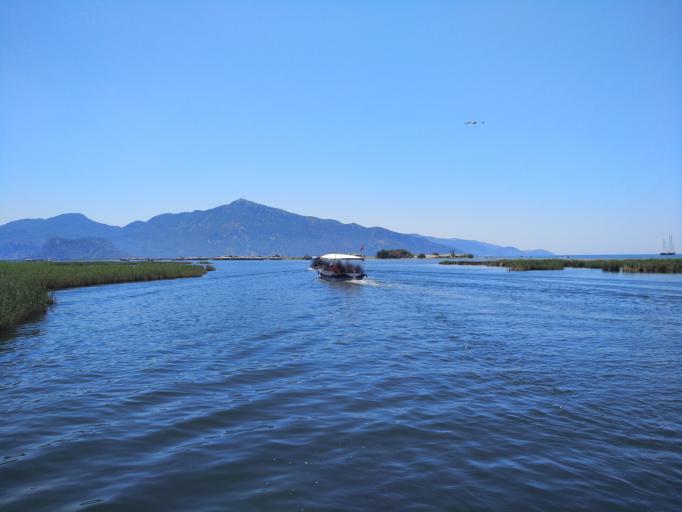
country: TR
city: Dalyan
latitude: 36.8057
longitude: 28.6036
